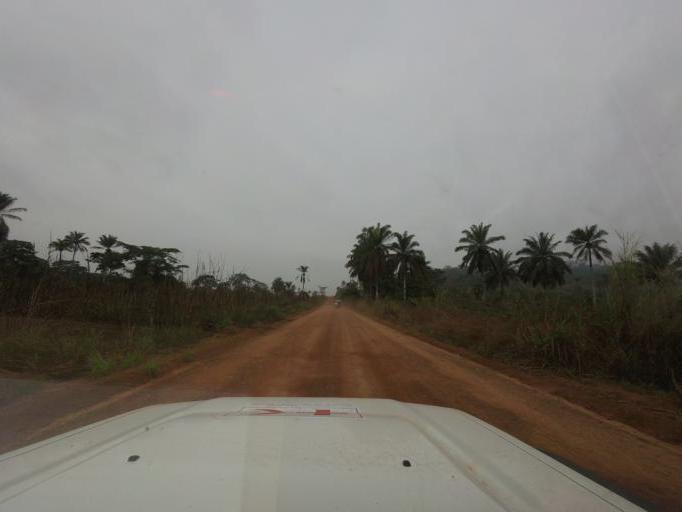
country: LR
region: Lofa
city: Voinjama
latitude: 8.3969
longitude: -9.7938
